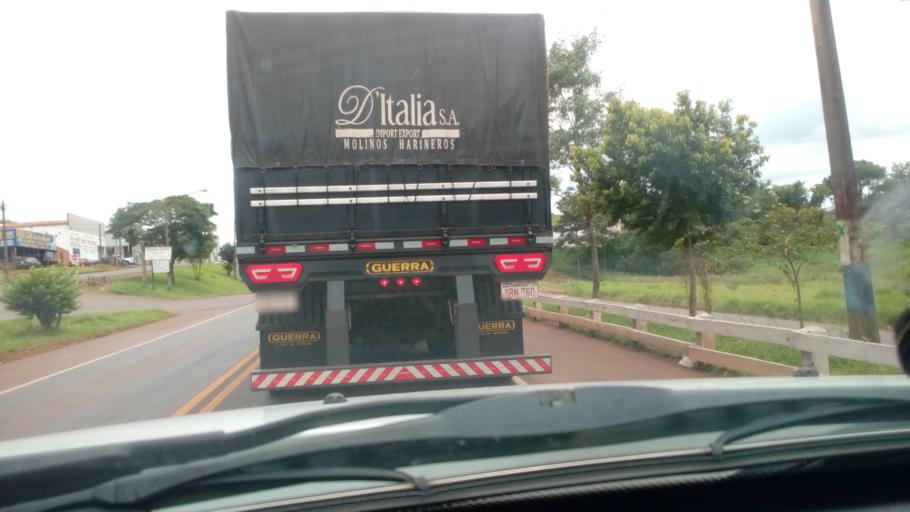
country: PY
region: Alto Parana
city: Santa Rita
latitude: -25.7903
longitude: -55.0844
